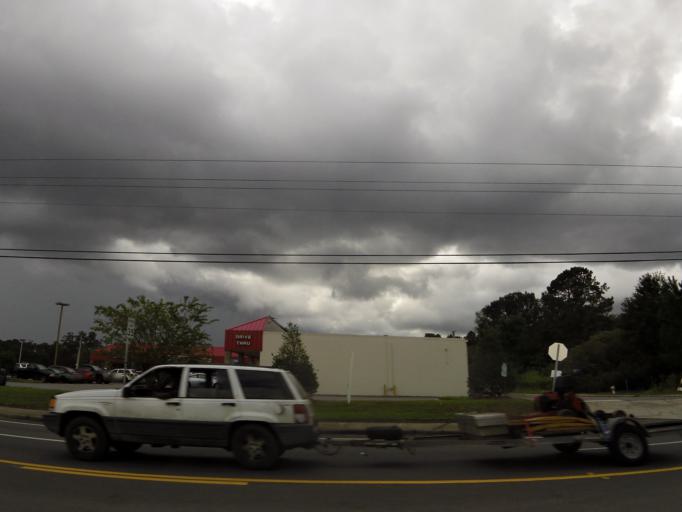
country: US
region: Florida
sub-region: Clay County
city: Middleburg
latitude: 30.0631
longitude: -81.8784
